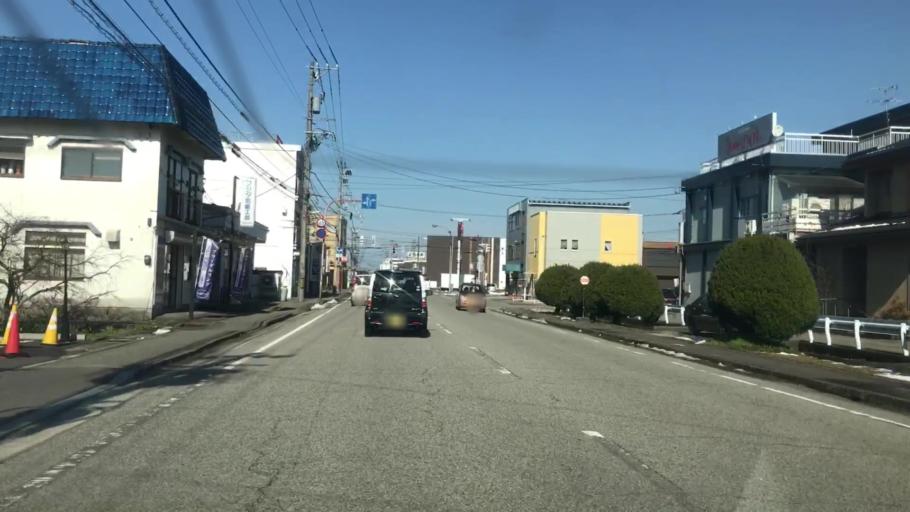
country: JP
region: Toyama
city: Toyama-shi
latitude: 36.6759
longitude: 137.2409
